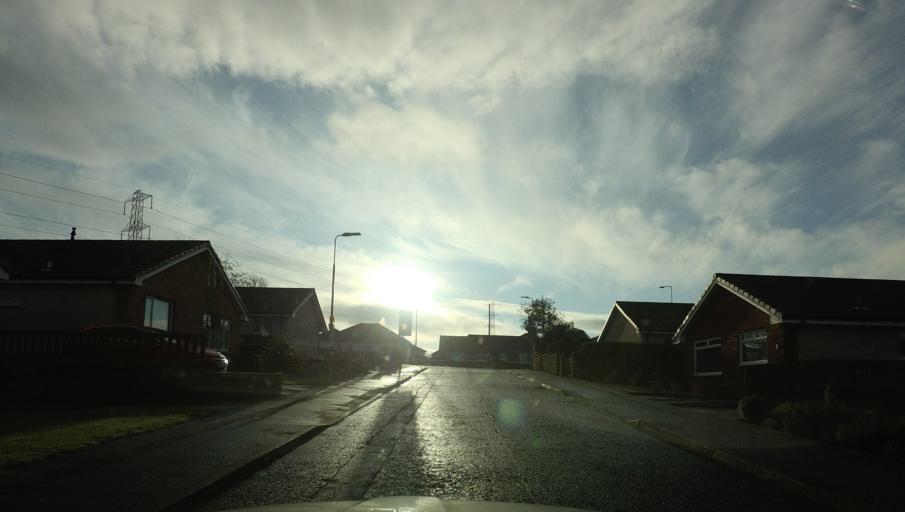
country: GB
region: Scotland
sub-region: West Lothian
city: Kirknewton
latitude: 55.8887
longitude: -3.4280
